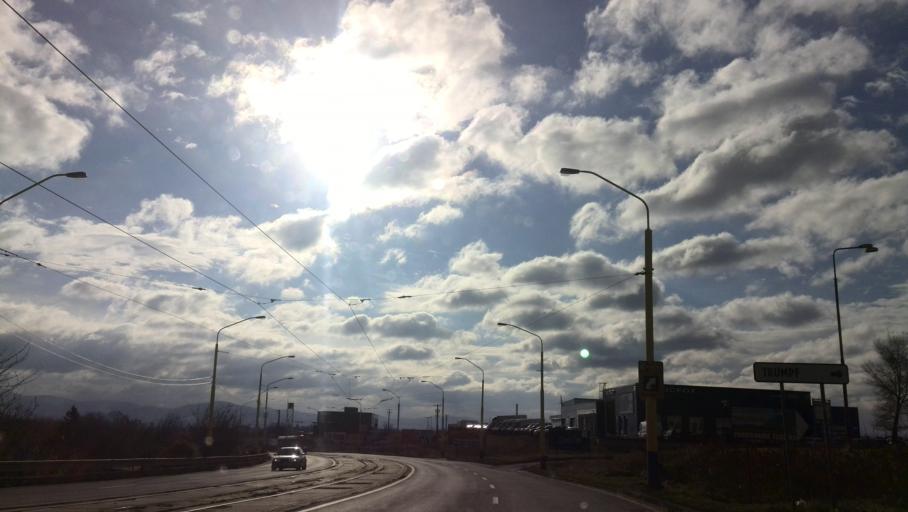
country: SK
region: Kosicky
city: Kosice
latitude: 48.6936
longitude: 21.2535
